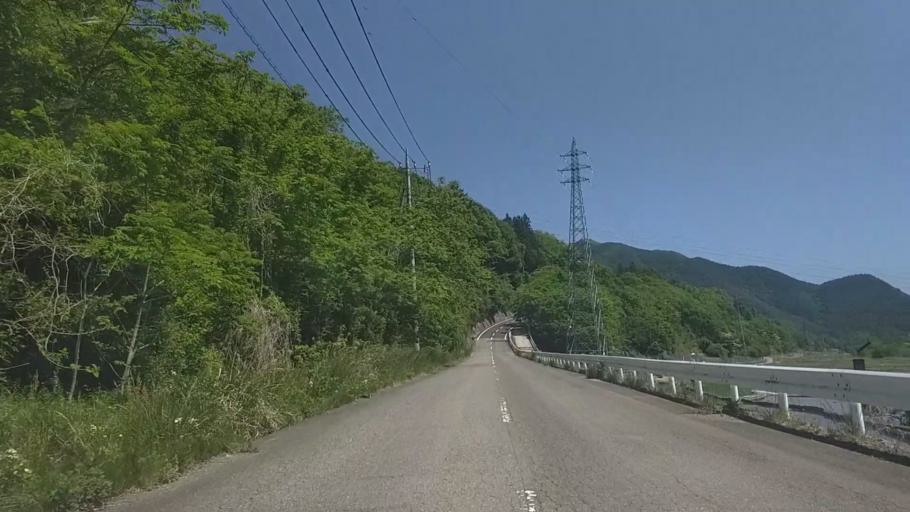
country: JP
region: Yamanashi
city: Nirasaki
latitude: 35.8543
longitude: 138.4357
